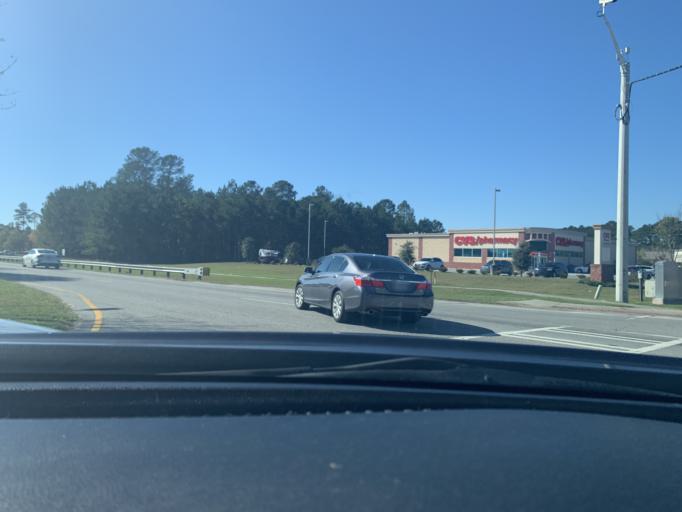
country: US
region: Georgia
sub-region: Chatham County
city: Pooler
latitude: 32.1353
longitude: -81.2544
